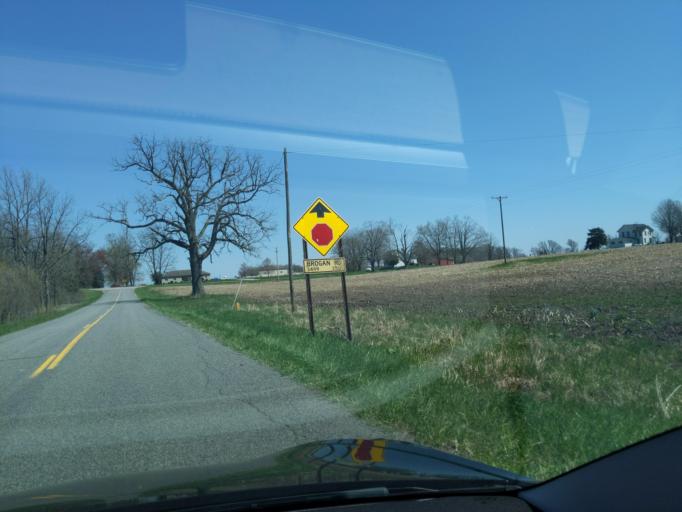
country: US
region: Michigan
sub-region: Ingham County
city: Stockbridge
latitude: 42.4830
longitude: -84.1625
